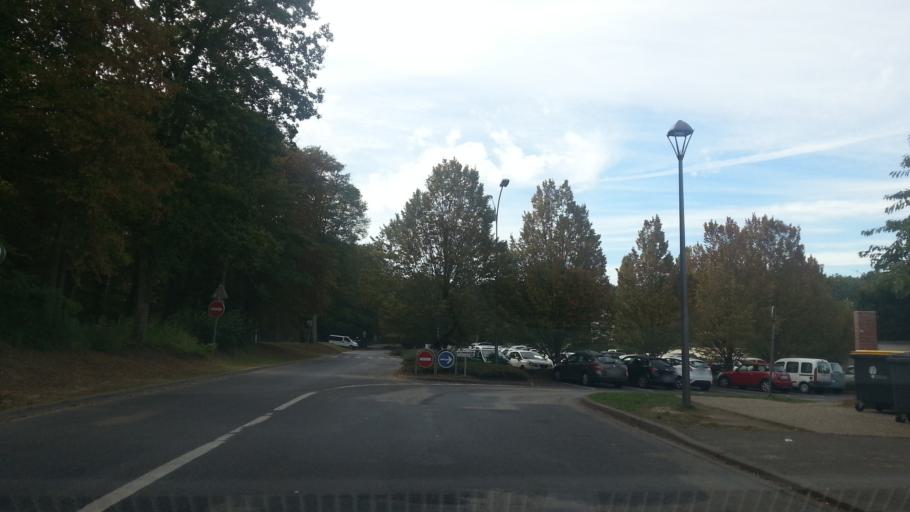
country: FR
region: Picardie
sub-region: Departement de l'Oise
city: Senlis
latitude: 49.1917
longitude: 2.5711
